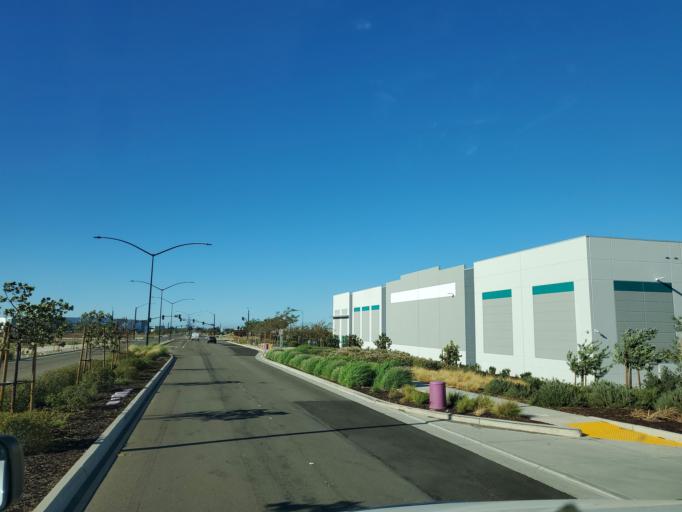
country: US
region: California
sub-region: San Joaquin County
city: Mountain House
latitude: 37.7231
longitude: -121.5131
